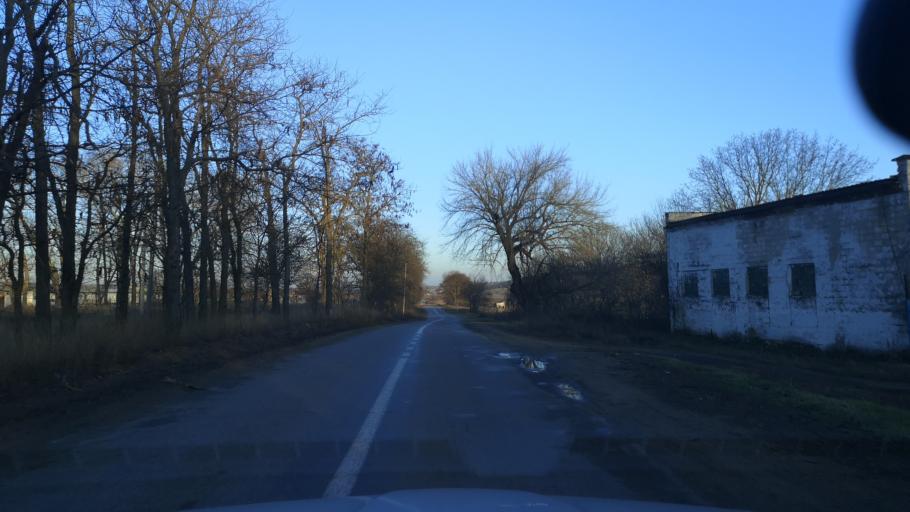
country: MD
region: Orhei
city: Orhei
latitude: 47.2934
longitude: 28.8945
